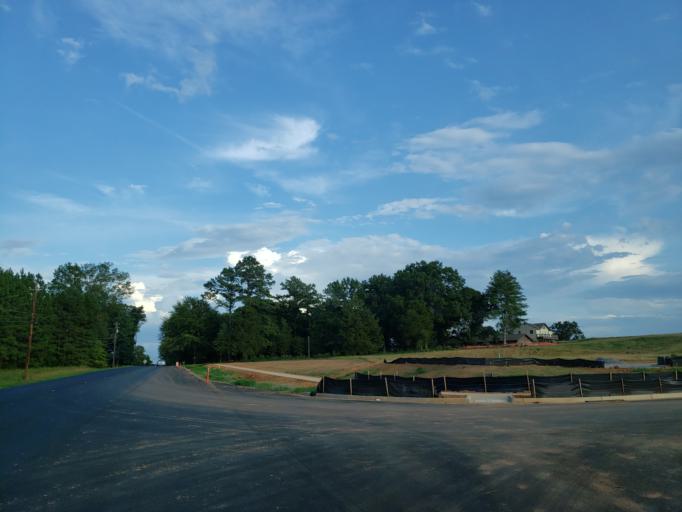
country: US
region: Georgia
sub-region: Bartow County
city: Cartersville
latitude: 34.2376
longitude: -84.8738
